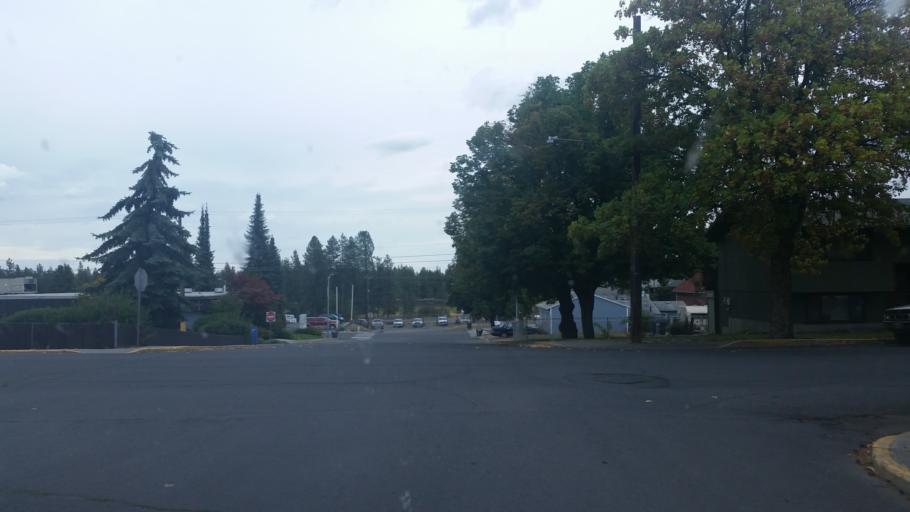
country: US
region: Washington
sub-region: Spokane County
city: Cheney
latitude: 47.4908
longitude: -117.5730
